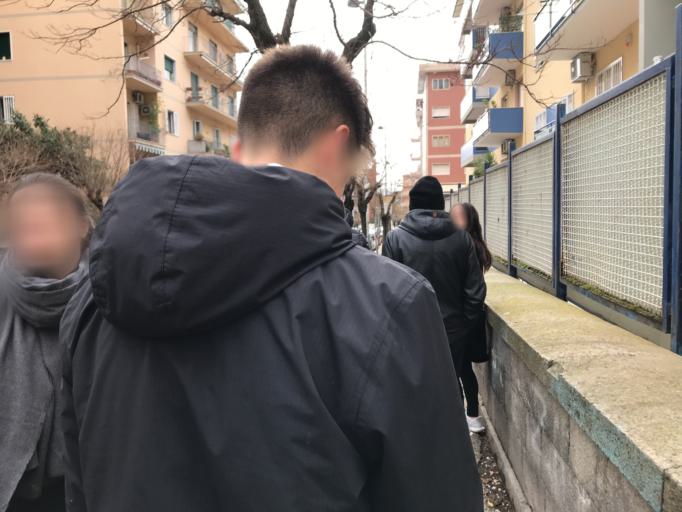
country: IT
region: Campania
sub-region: Provincia di Napoli
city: Napoli
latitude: 40.8575
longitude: 14.2284
